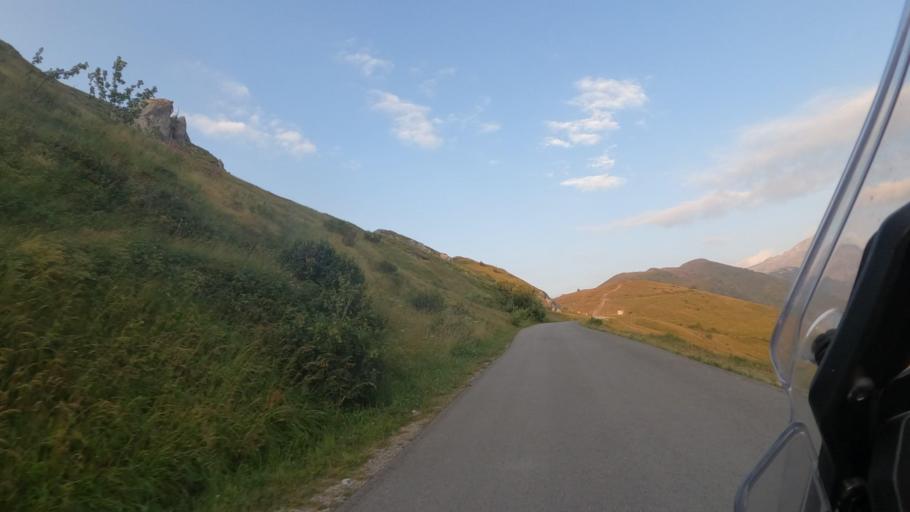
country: IT
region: Piedmont
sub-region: Provincia di Cuneo
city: Limone Piemonte
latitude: 44.1508
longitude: 7.5638
